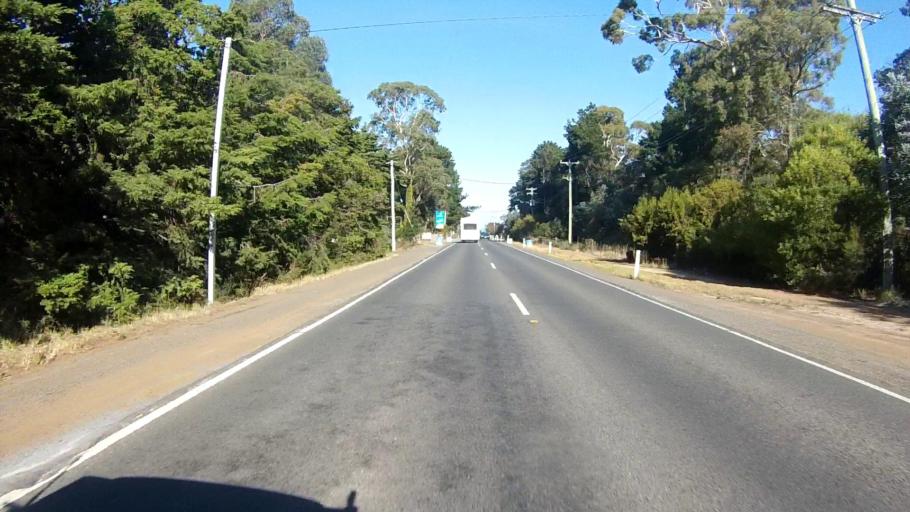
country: AU
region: Tasmania
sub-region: Clarence
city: Cambridge
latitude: -42.8380
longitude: 147.4644
